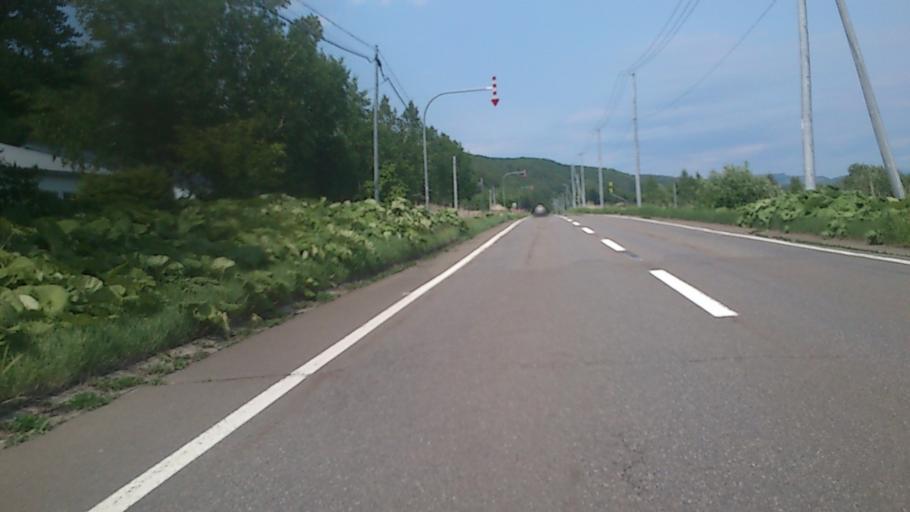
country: JP
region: Hokkaido
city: Otofuke
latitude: 43.2567
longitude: 143.5702
